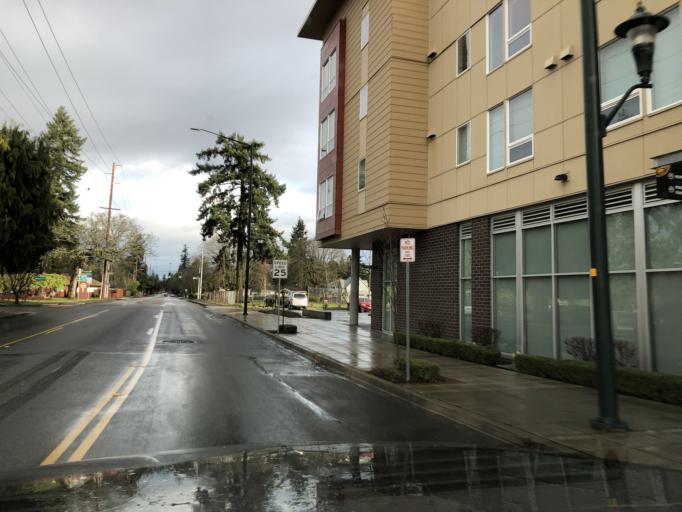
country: US
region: Washington
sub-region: Pierce County
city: Parkland
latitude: 47.1464
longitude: -122.4371
